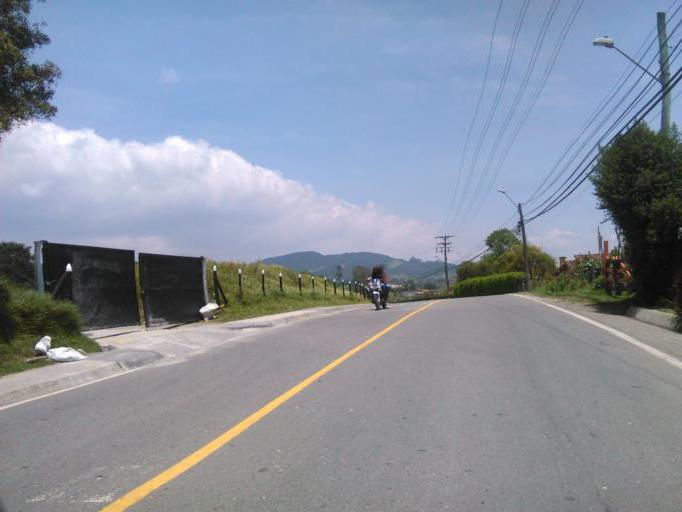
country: CO
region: Antioquia
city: La Union
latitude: 5.9782
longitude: -75.3665
